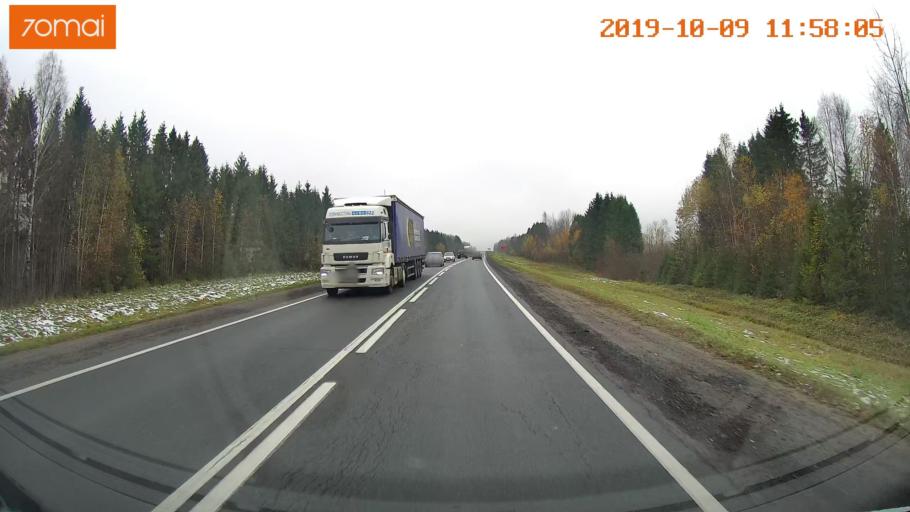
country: RU
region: Vologda
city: Gryazovets
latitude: 58.7233
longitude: 40.2959
